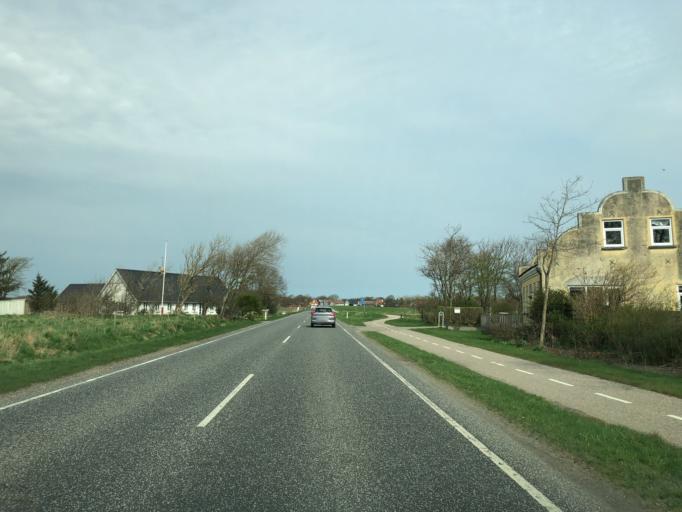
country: DK
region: Central Jutland
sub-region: Ringkobing-Skjern Kommune
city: Skjern
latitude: 55.8992
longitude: 8.4327
